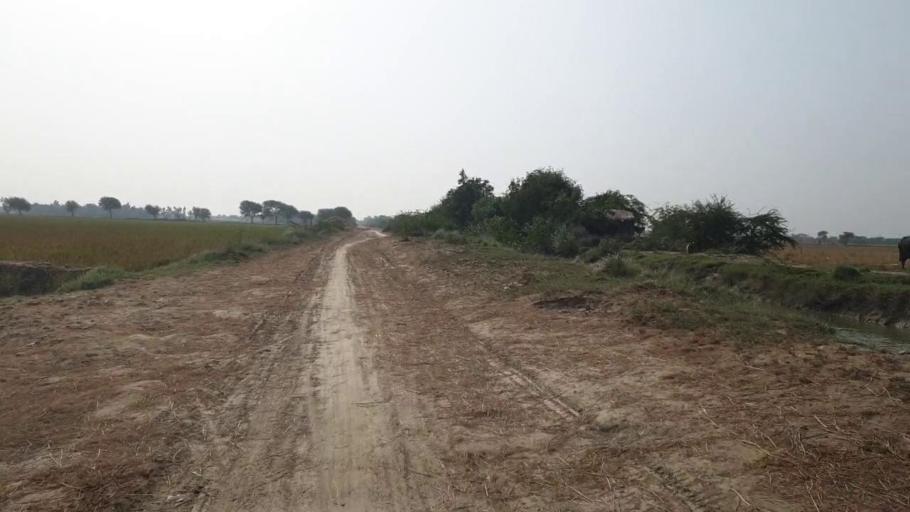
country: PK
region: Sindh
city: Kario
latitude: 24.7628
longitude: 68.5637
